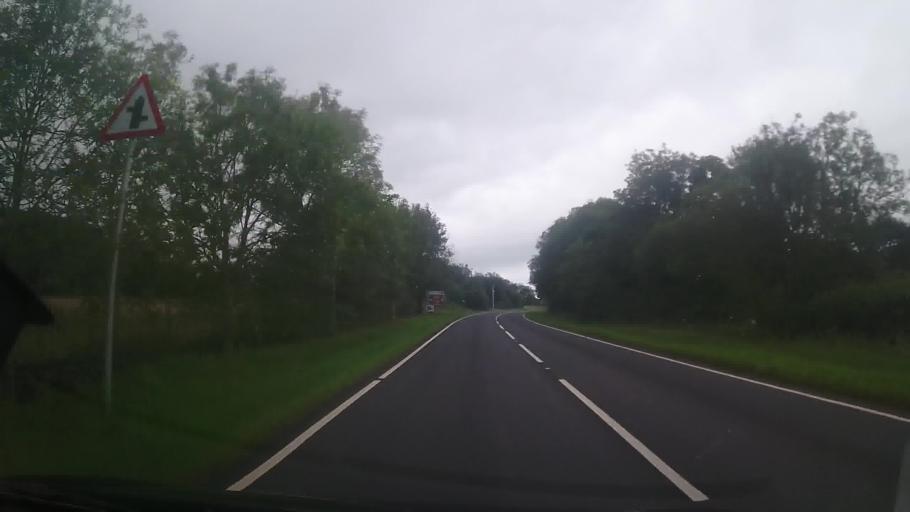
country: GB
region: Wales
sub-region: Gwynedd
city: Caernarfon
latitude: 53.1658
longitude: -4.3125
